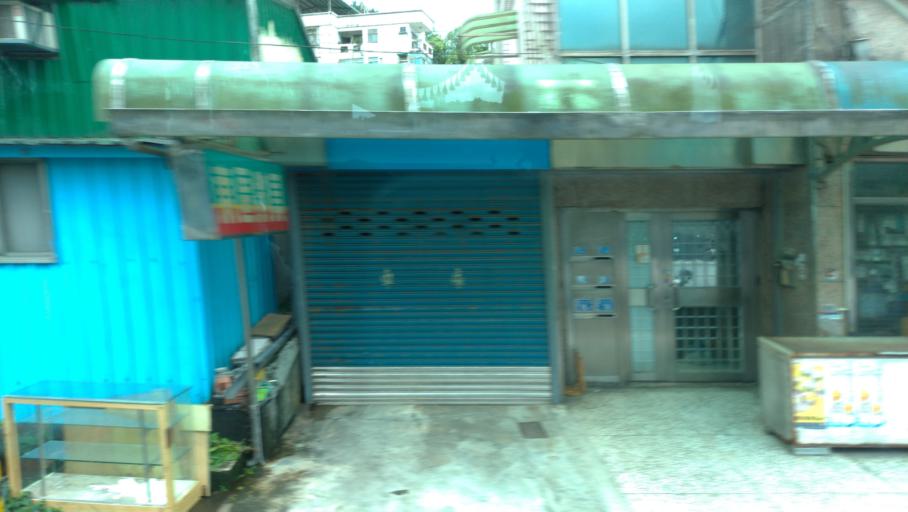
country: TW
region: Taiwan
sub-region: Keelung
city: Keelung
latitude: 25.1026
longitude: 121.7394
